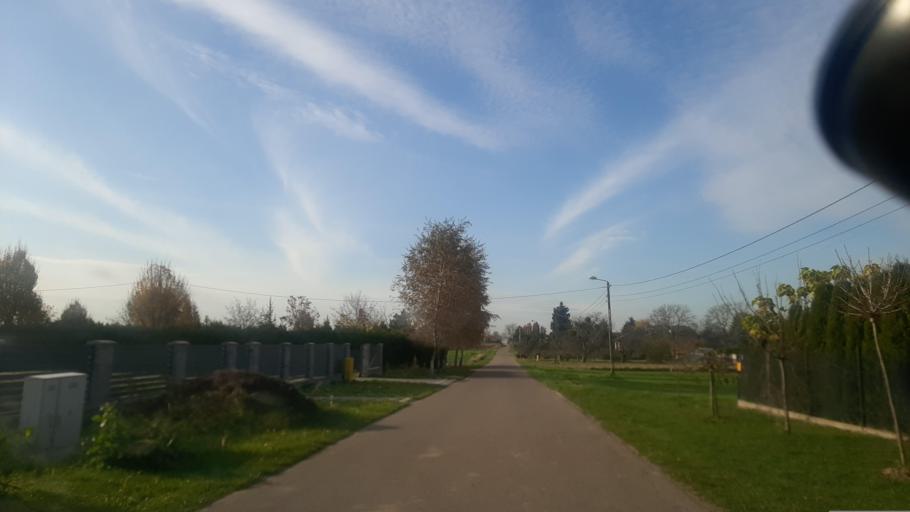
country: PL
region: Lublin Voivodeship
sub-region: Powiat pulawski
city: Markuszow
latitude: 51.3638
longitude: 22.2880
